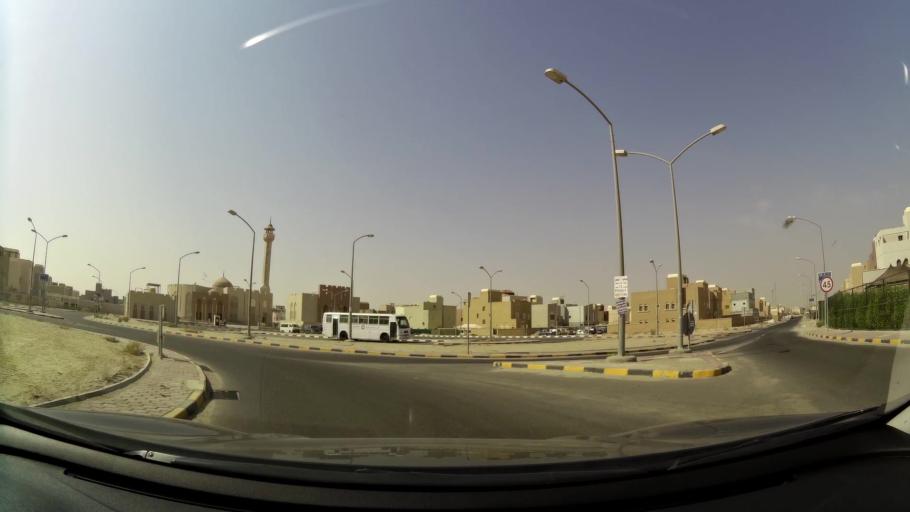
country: KW
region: Al Ahmadi
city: Al Wafrah
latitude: 28.8030
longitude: 48.0575
